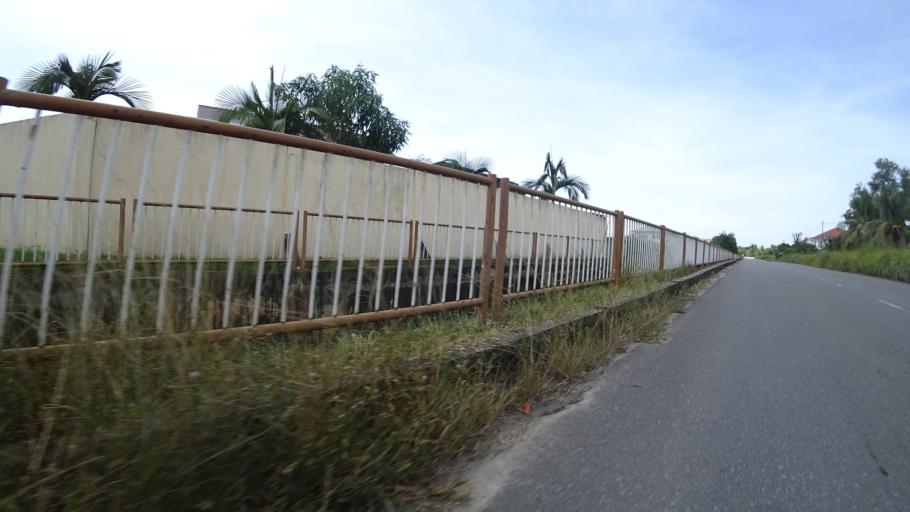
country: BN
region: Brunei and Muara
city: Bandar Seri Begawan
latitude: 4.8855
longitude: 114.8533
